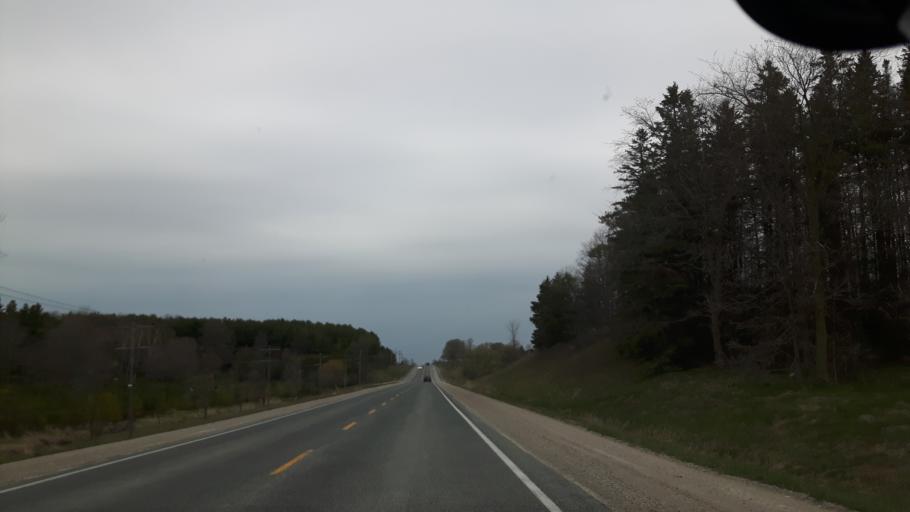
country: CA
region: Ontario
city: Goderich
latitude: 43.6681
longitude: -81.6218
